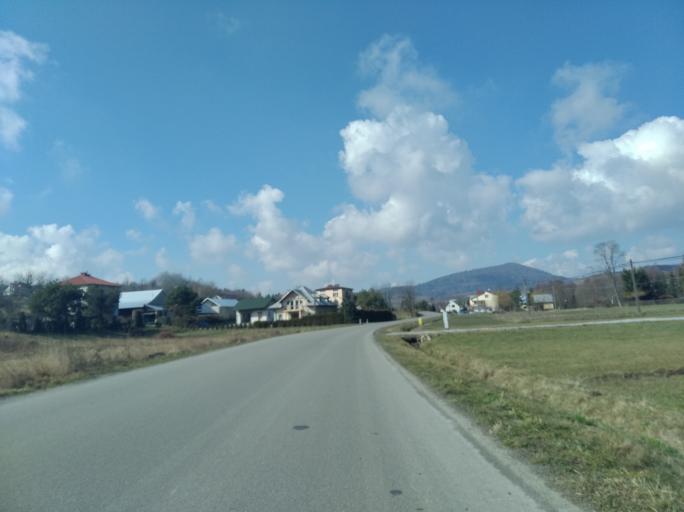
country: PL
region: Subcarpathian Voivodeship
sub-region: Powiat strzyzowski
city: Frysztak
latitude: 49.8700
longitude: 21.6009
